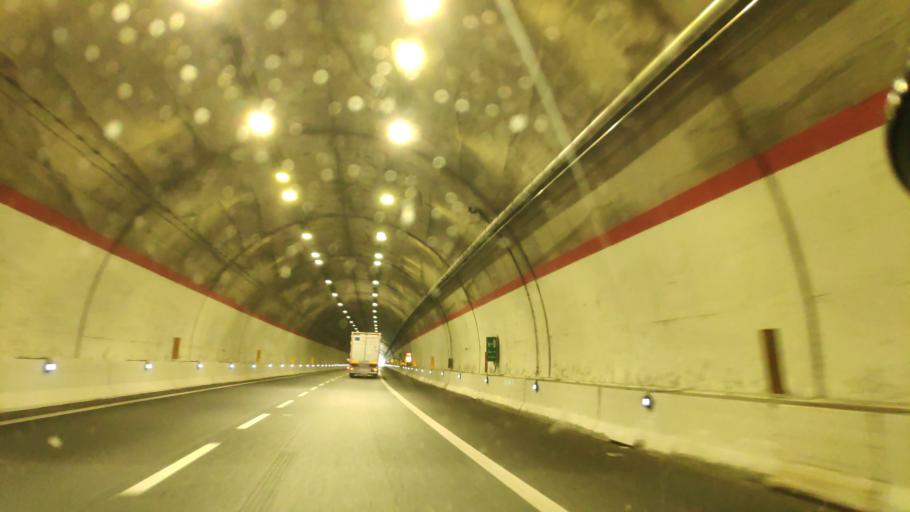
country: IT
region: Campania
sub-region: Provincia di Salerno
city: Sicignano degli Alburni
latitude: 40.5818
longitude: 15.3430
